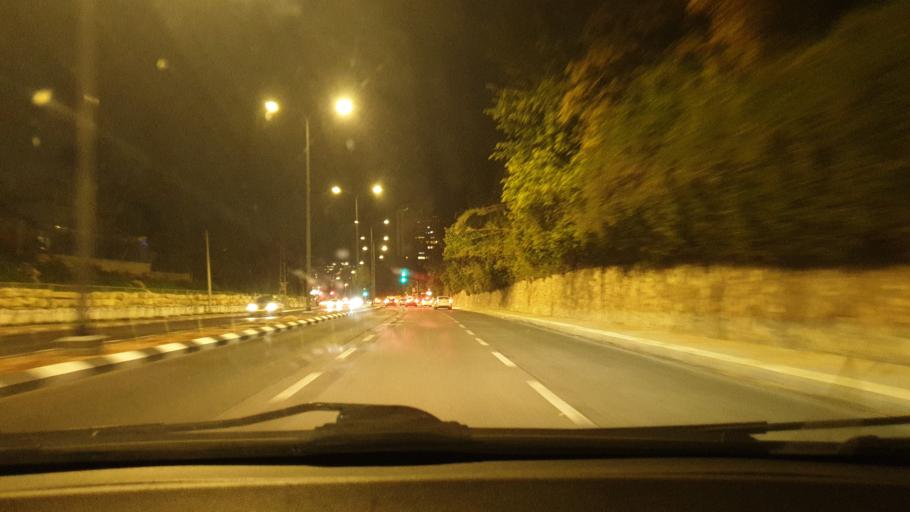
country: IL
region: Tel Aviv
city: Ramat Gan
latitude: 32.1204
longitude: 34.8068
